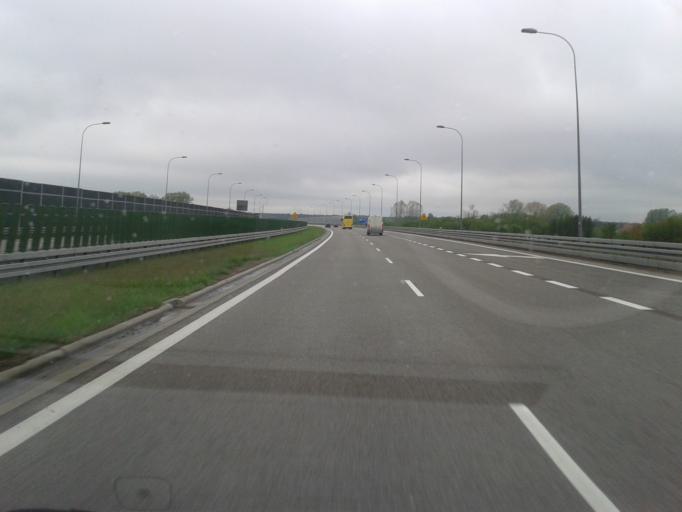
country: PL
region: Subcarpathian Voivodeship
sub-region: Powiat debicki
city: Brzeznica
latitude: 50.0964
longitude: 21.5147
